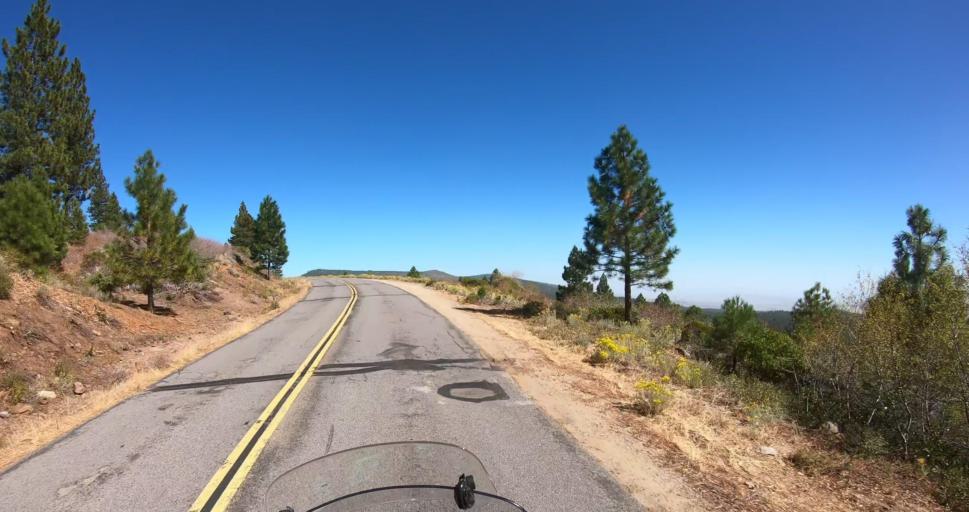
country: US
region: California
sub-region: Lassen County
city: Susanville
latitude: 40.4739
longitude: -120.7519
